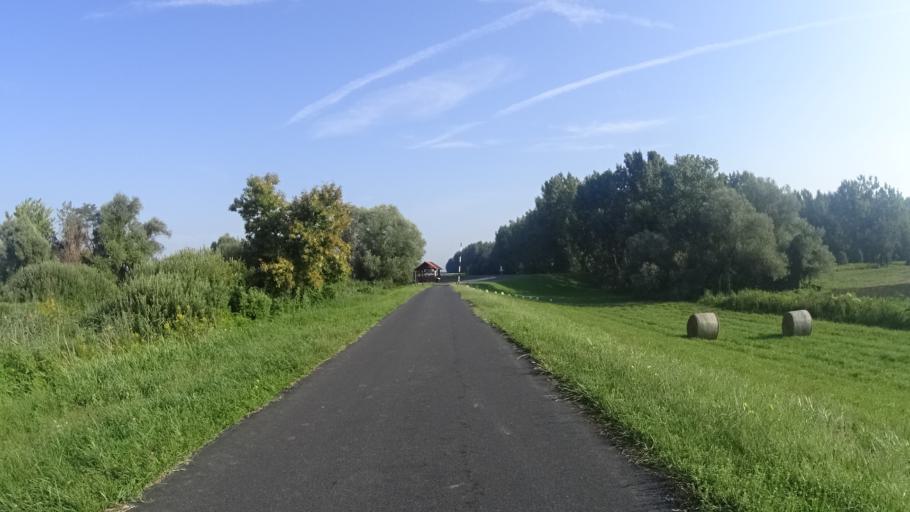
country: HU
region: Zala
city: Sarmellek
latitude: 46.6602
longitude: 17.1337
